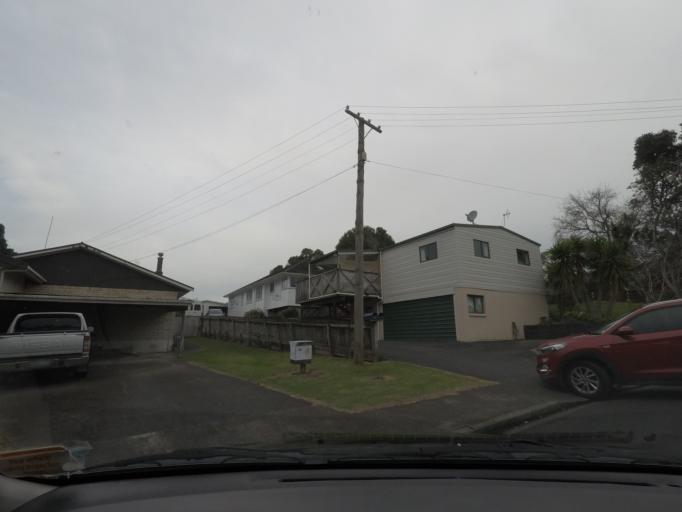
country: NZ
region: Auckland
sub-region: Auckland
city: Rosebank
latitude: -36.8609
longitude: 174.6420
